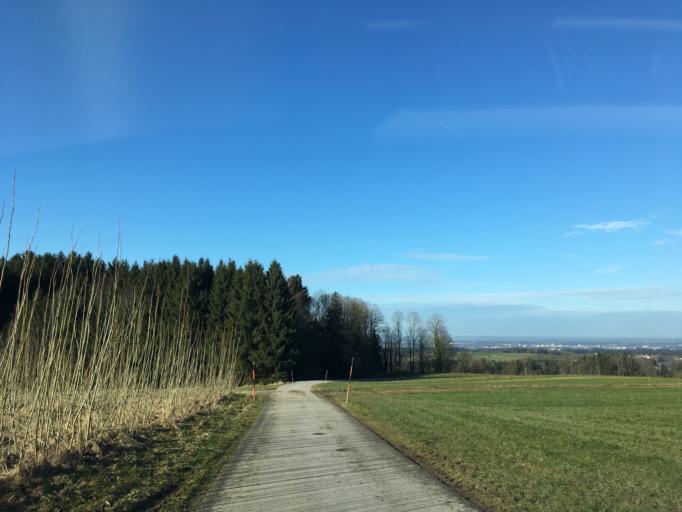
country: DE
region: Bavaria
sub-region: Upper Bavaria
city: Riedering
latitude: 47.8092
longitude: 12.2292
